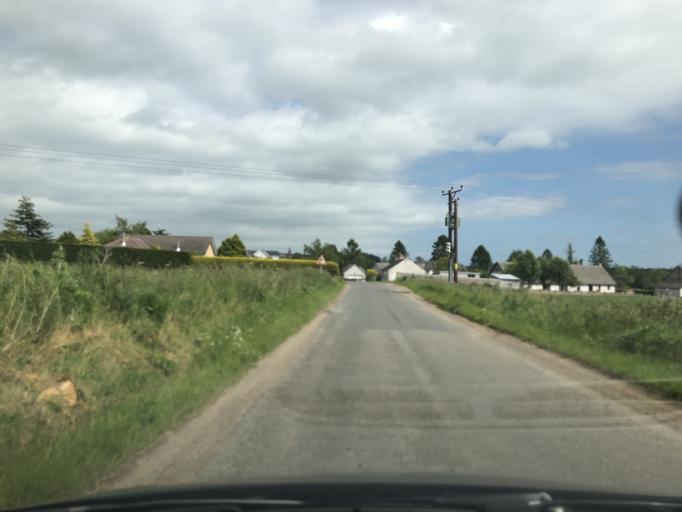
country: GB
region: Scotland
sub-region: Angus
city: Kirriemuir
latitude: 56.7207
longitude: -2.9414
